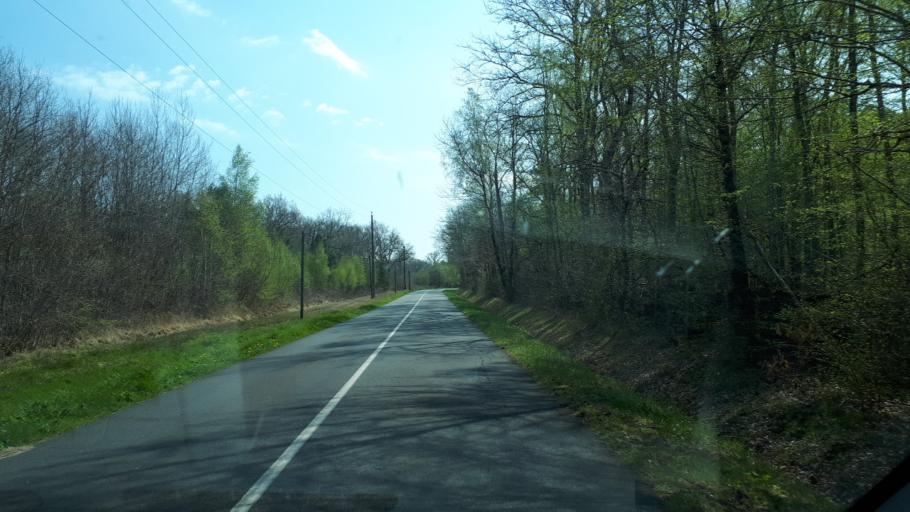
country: FR
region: Centre
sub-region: Departement du Loir-et-Cher
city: Selles-Saint-Denis
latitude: 47.3426
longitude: 1.8982
